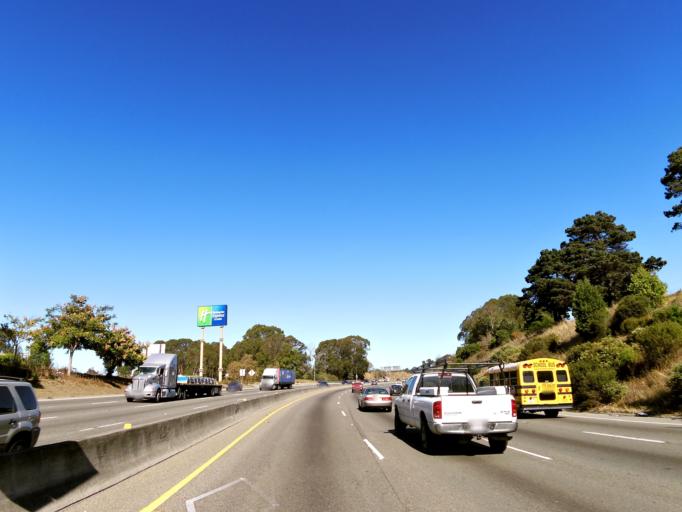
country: US
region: California
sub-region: Contra Costa County
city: Rollingwood
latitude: 37.9562
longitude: -122.3300
